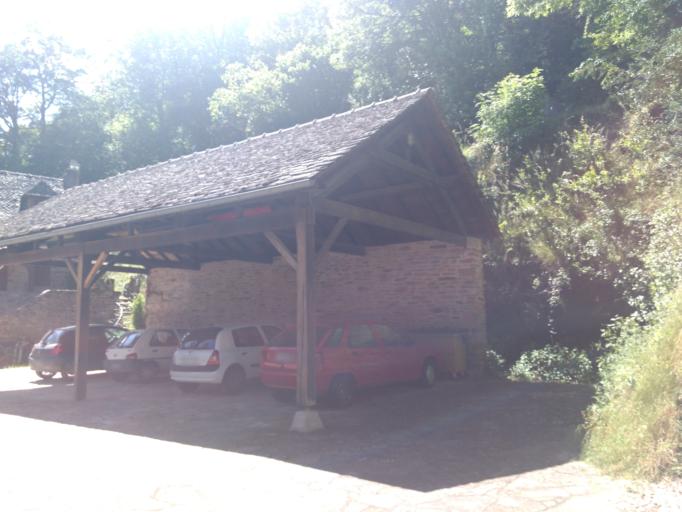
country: FR
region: Midi-Pyrenees
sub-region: Departement de l'Aveyron
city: Colombies
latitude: 44.3880
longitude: 2.3352
